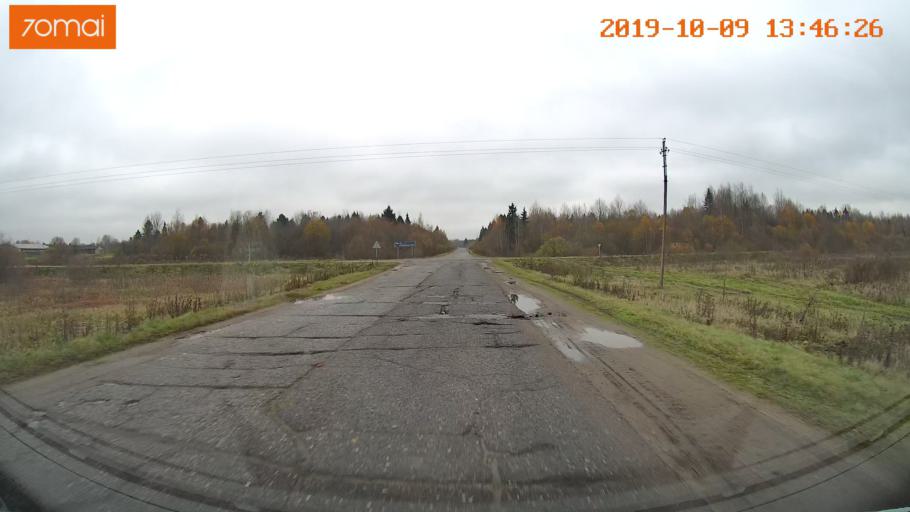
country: RU
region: Kostroma
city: Buy
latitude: 58.3838
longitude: 41.2180
